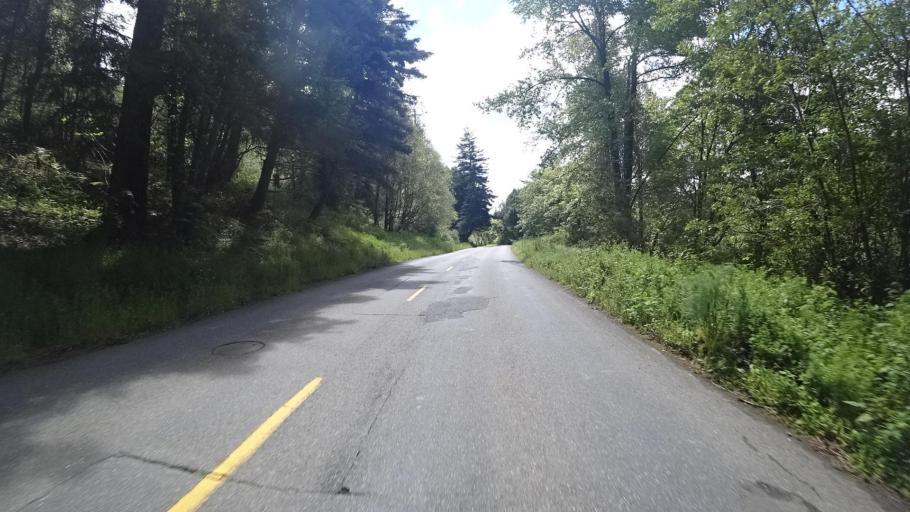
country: US
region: California
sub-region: Humboldt County
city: Blue Lake
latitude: 40.9048
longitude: -124.0330
